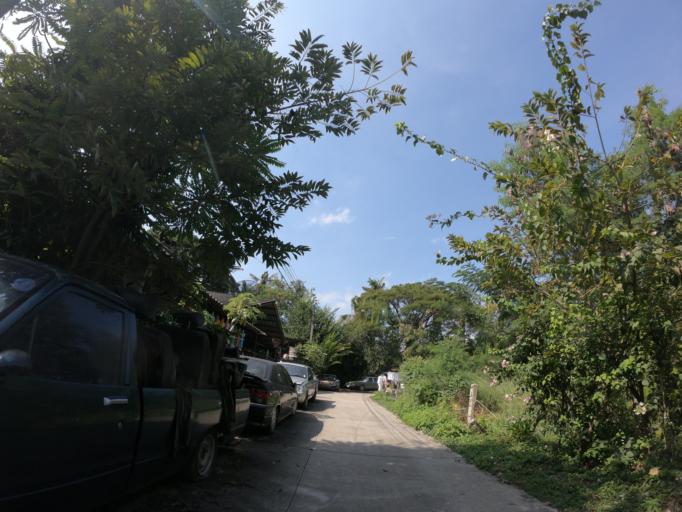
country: TH
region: Chiang Mai
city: Chiang Mai
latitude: 18.7737
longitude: 99.0305
